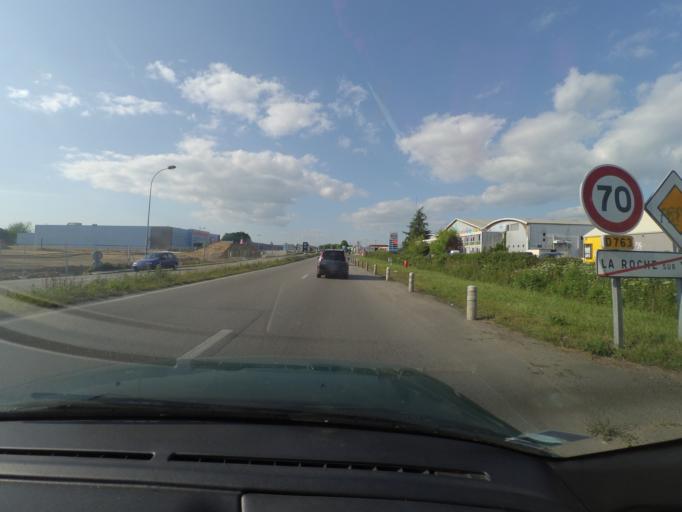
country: FR
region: Pays de la Loire
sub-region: Departement de la Vendee
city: La Roche-sur-Yon
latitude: 46.6910
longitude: -1.4298
